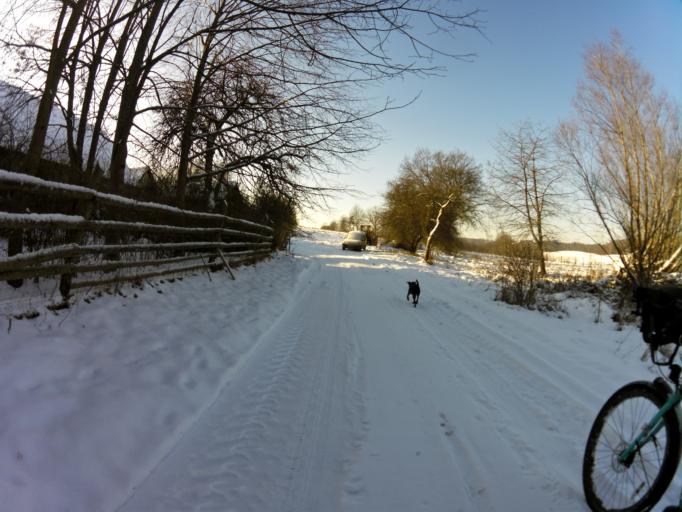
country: PL
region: West Pomeranian Voivodeship
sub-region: Powiat stargardzki
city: Dobrzany
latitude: 53.3870
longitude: 15.4883
